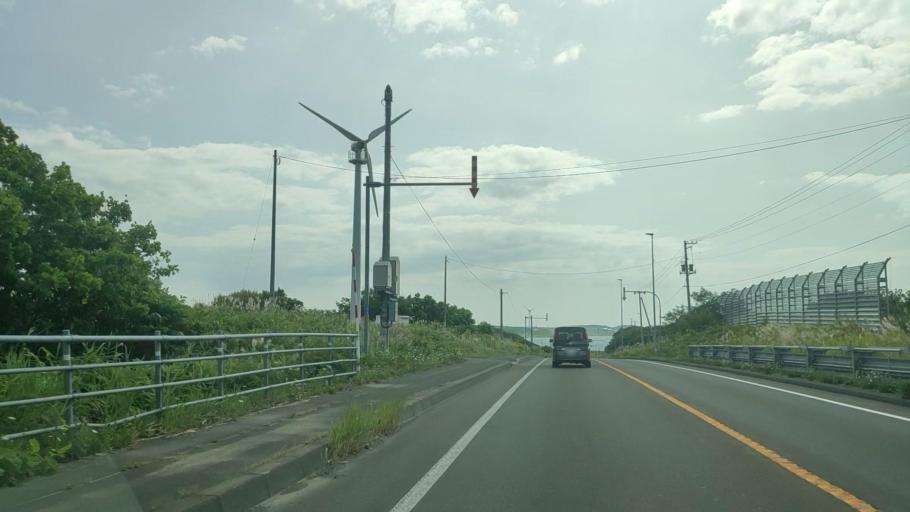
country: JP
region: Hokkaido
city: Rumoi
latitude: 44.3410
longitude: 141.6851
